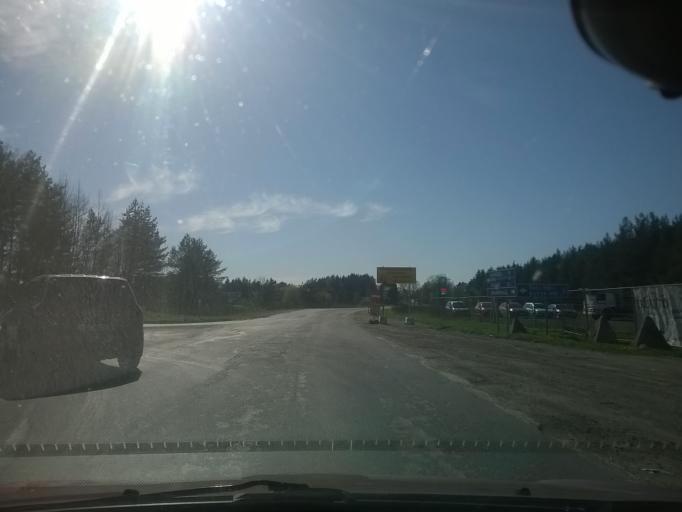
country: EE
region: Harju
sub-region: Tallinna linn
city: Kose
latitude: 59.4613
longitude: 24.9170
